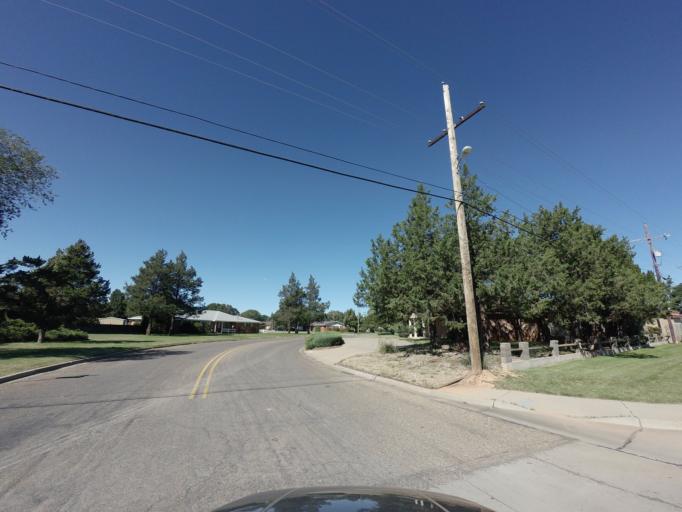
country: US
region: New Mexico
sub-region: Curry County
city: Clovis
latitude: 34.4204
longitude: -103.1877
